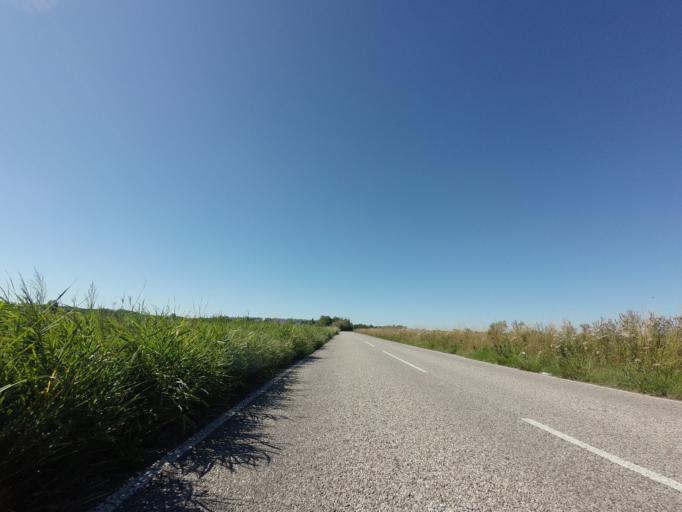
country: GB
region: England
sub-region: Kent
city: Ash
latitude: 51.3181
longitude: 1.2145
